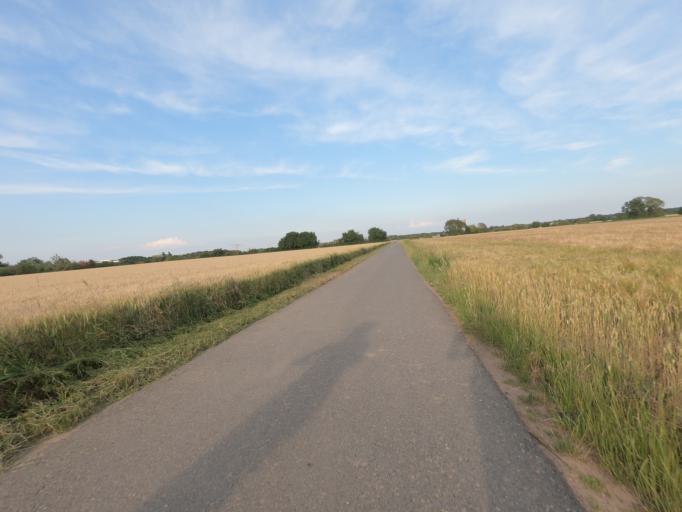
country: DE
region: Hesse
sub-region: Regierungsbezirk Darmstadt
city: Russelsheim
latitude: 49.9697
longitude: 8.4299
